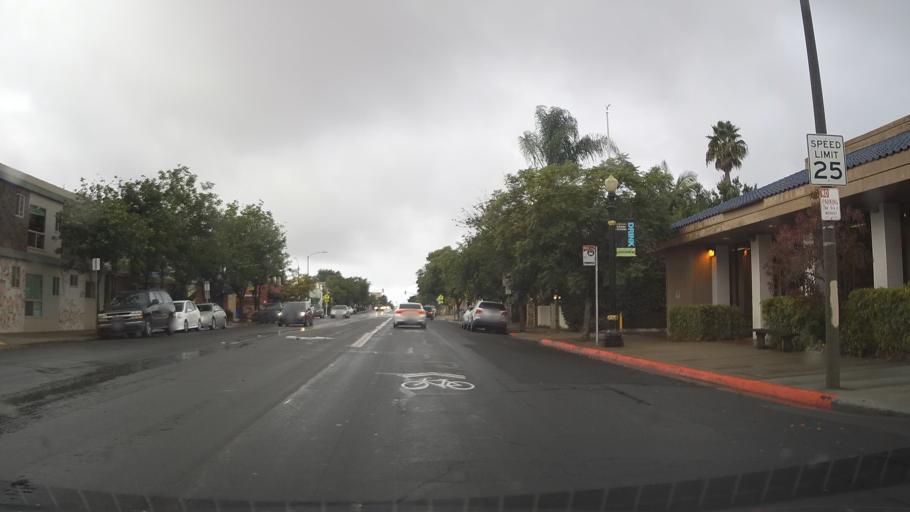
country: US
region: California
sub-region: San Diego County
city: San Diego
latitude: 32.7633
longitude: -117.1110
